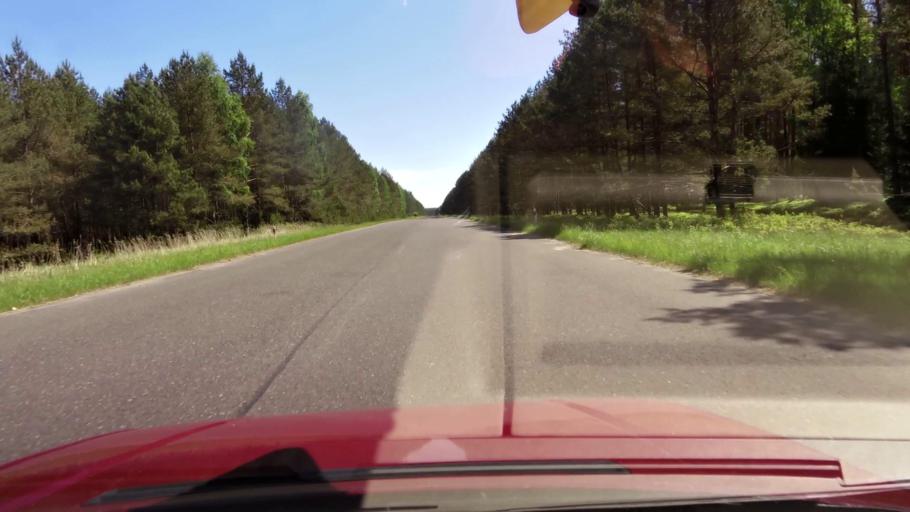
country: PL
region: West Pomeranian Voivodeship
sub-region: Powiat koszalinski
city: Bobolice
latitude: 54.0693
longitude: 16.5380
